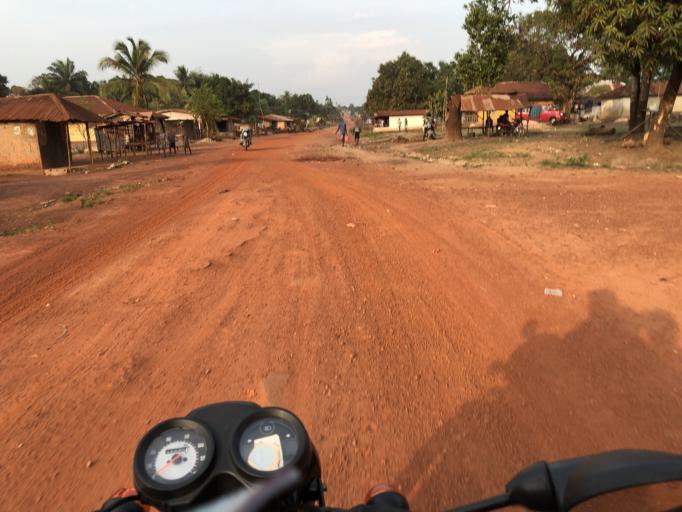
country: SL
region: Northern Province
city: Yonibana
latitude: 8.4671
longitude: -12.2095
